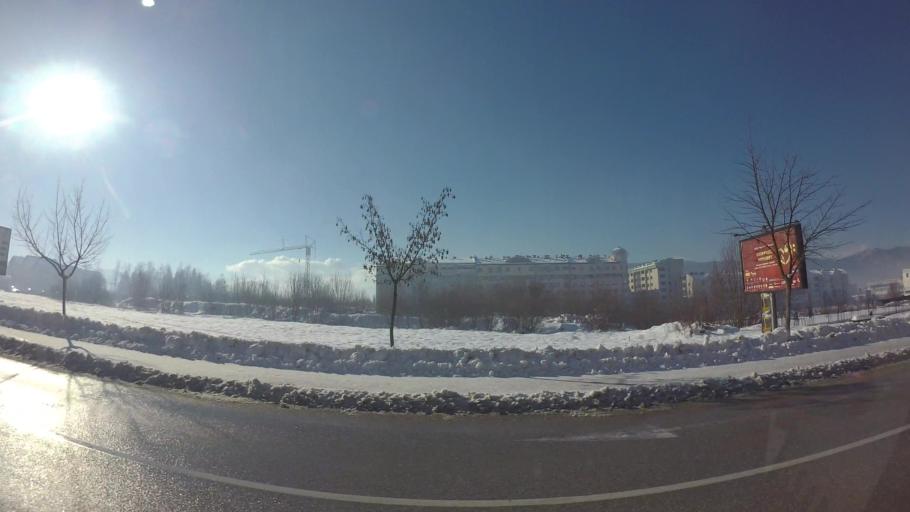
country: BA
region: Federation of Bosnia and Herzegovina
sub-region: Kanton Sarajevo
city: Sarajevo
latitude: 43.8222
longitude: 18.3674
